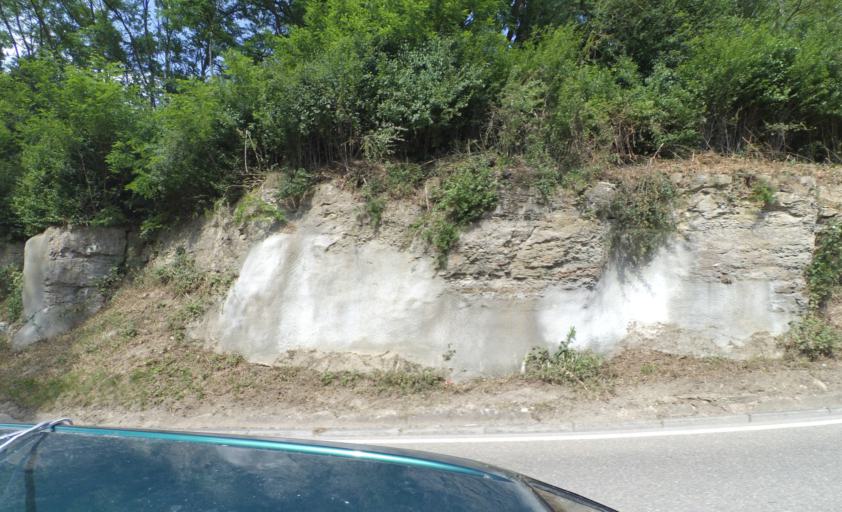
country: DE
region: Baden-Wuerttemberg
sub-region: Regierungsbezirk Stuttgart
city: Huttlingen
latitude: 48.8786
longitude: 10.0994
